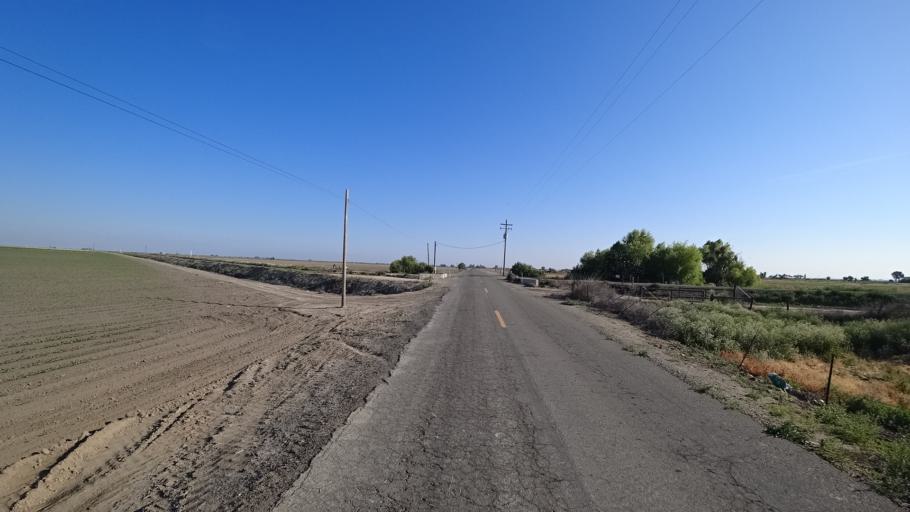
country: US
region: California
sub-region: Fresno County
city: Riverdale
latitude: 36.3902
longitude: -119.9278
